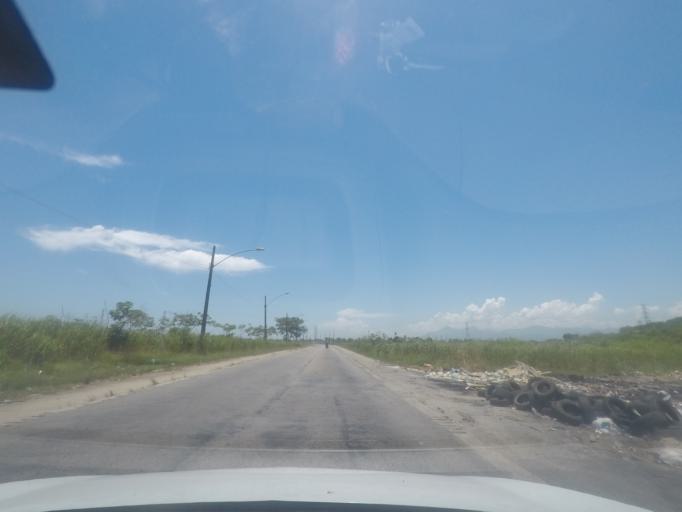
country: BR
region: Rio de Janeiro
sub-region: Itaguai
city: Itaguai
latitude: -22.8959
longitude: -43.6829
